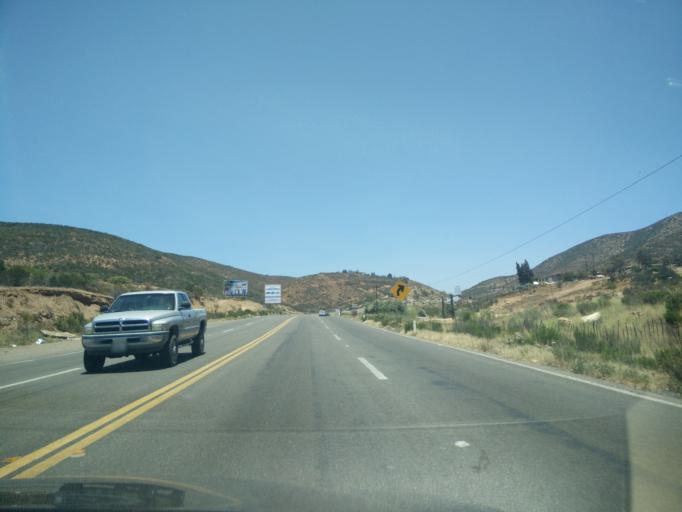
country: MX
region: Baja California
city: El Sauzal
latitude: 31.9495
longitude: -116.6663
